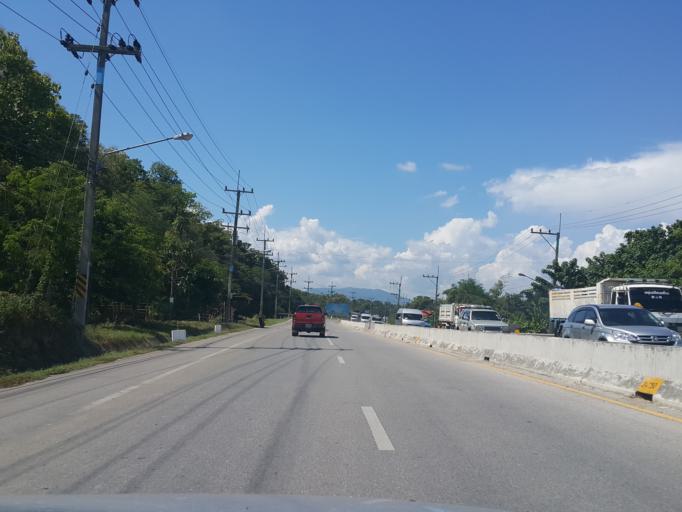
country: TH
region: Chiang Mai
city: Mae Taeng
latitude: 19.0501
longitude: 98.9458
